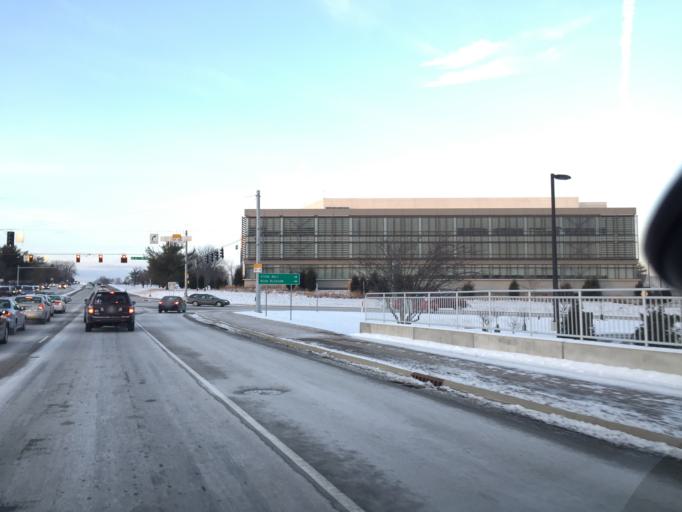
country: US
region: Indiana
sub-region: Monroe County
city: Bloomington
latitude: 39.1709
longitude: -86.5018
